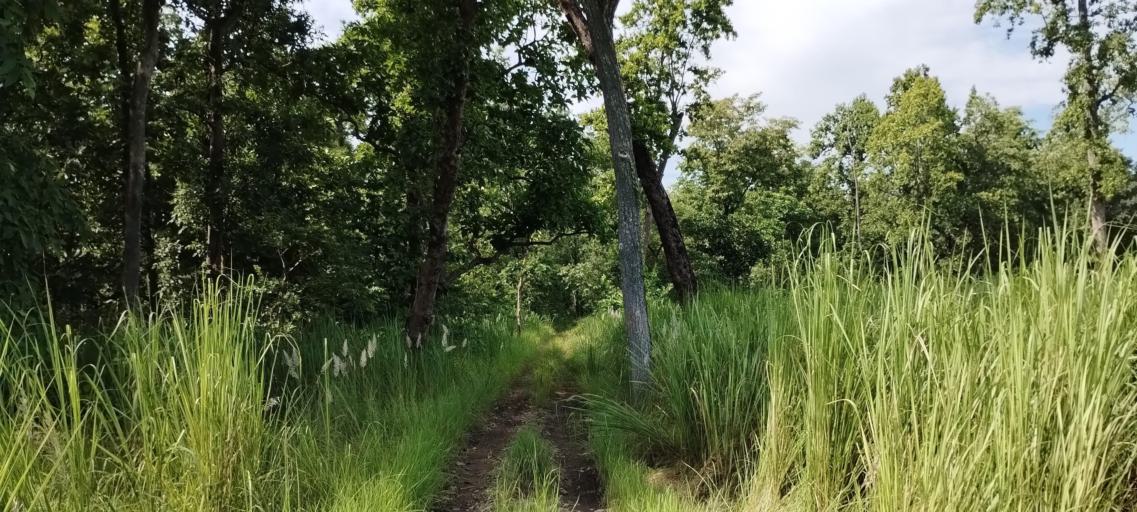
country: NP
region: Far Western
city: Tikapur
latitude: 28.5609
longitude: 81.2948
